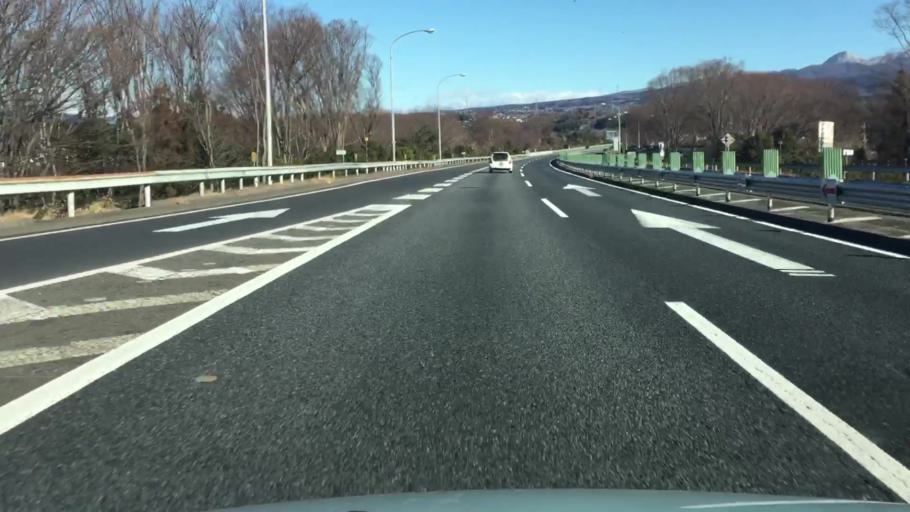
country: JP
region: Gunma
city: Shibukawa
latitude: 36.4761
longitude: 139.0158
